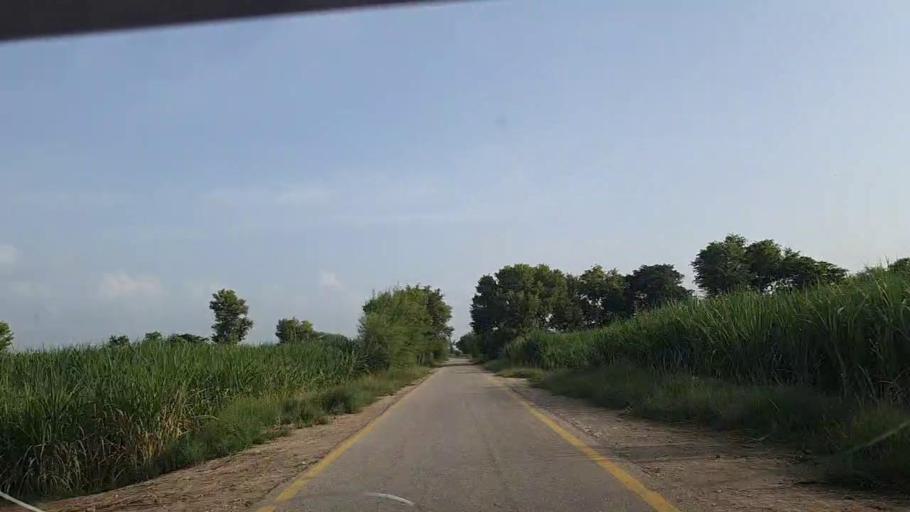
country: PK
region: Sindh
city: Adilpur
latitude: 27.9684
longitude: 69.2560
